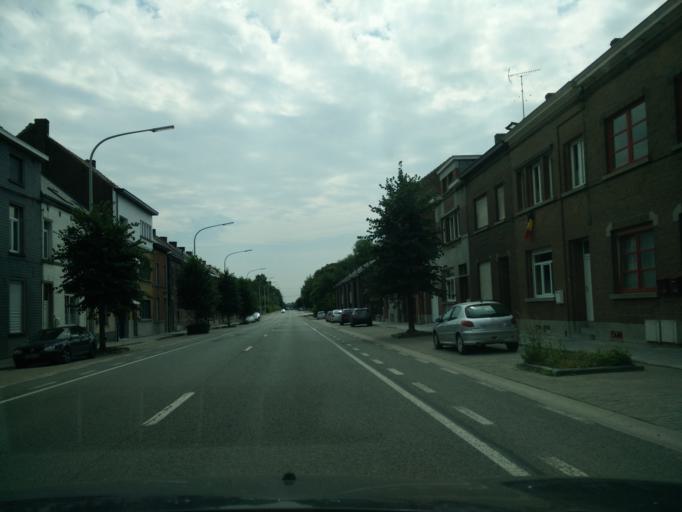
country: BE
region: Wallonia
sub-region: Province du Hainaut
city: Soignies
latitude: 50.5691
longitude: 4.0695
